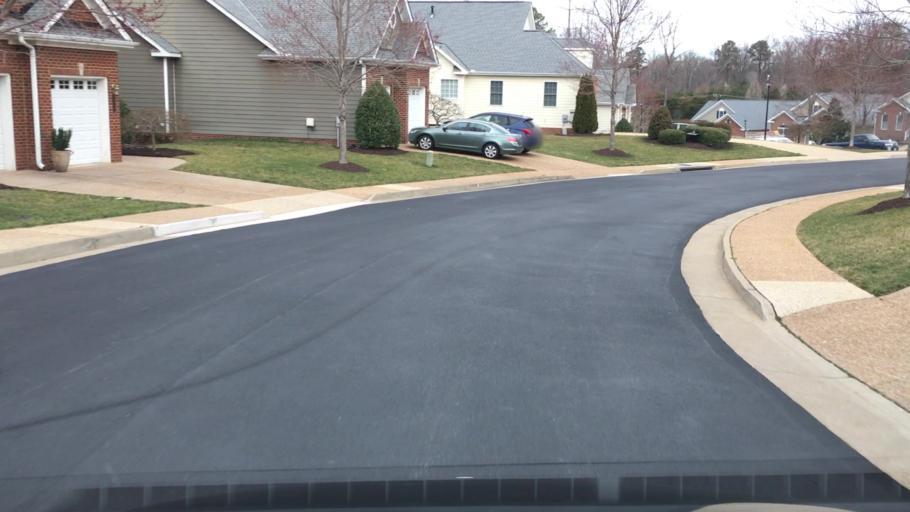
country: US
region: Virginia
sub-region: Chesterfield County
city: Bon Air
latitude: 37.5426
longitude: -77.5576
